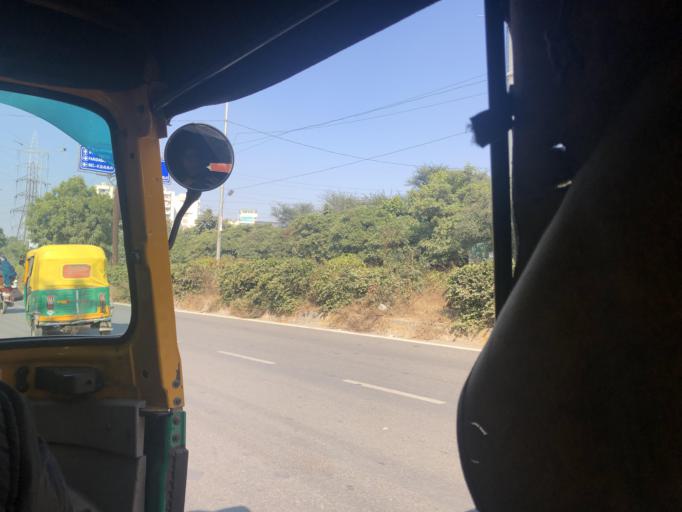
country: IN
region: Haryana
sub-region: Gurgaon
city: Gurgaon
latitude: 28.4463
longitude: 77.0806
